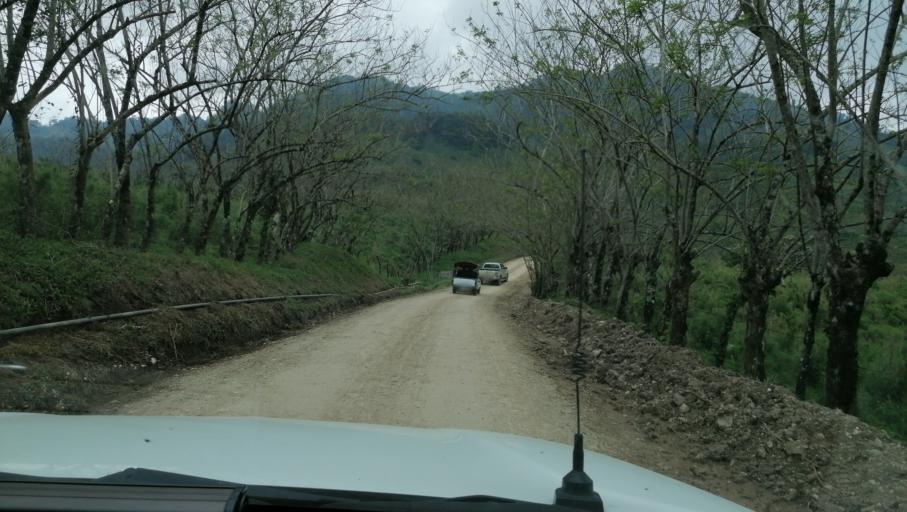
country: MX
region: Chiapas
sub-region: Ocotepec
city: San Pablo Huacano
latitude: 17.2686
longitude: -93.2598
